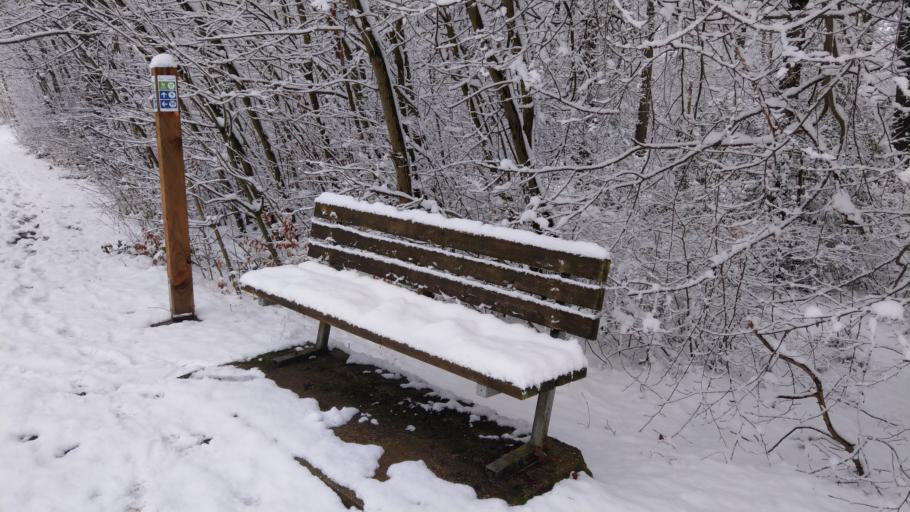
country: BE
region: Wallonia
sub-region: Province de Liege
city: Lontzen
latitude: 50.6895
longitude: 6.0516
